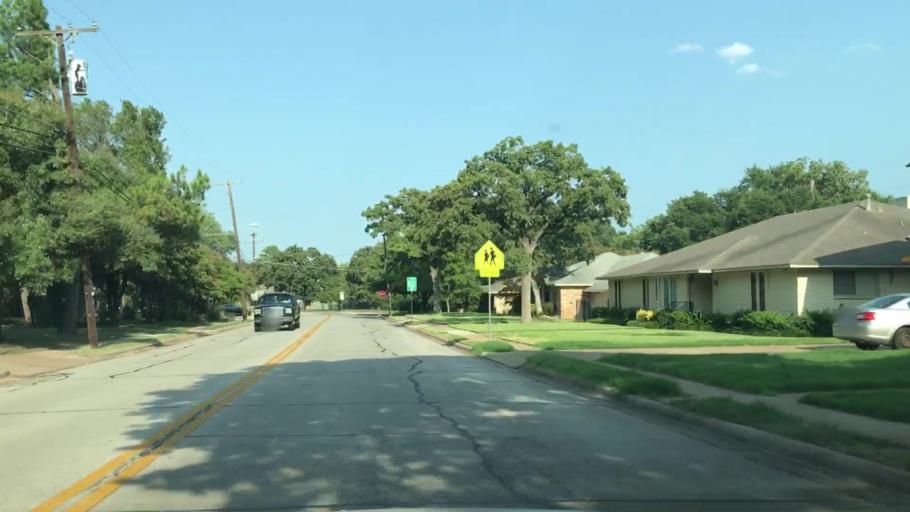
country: US
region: Texas
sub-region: Dallas County
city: Irving
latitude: 32.8230
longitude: -96.9270
